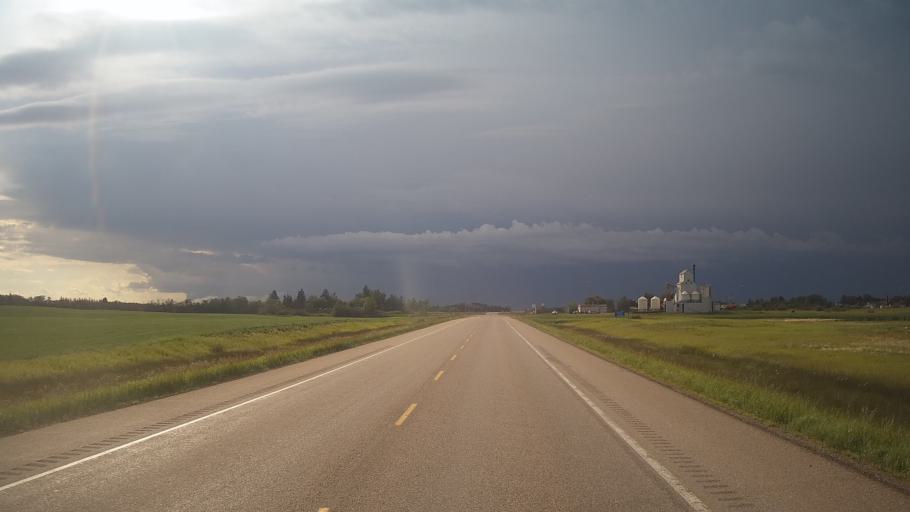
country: CA
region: Alberta
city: Vegreville
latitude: 53.2263
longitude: -112.2323
